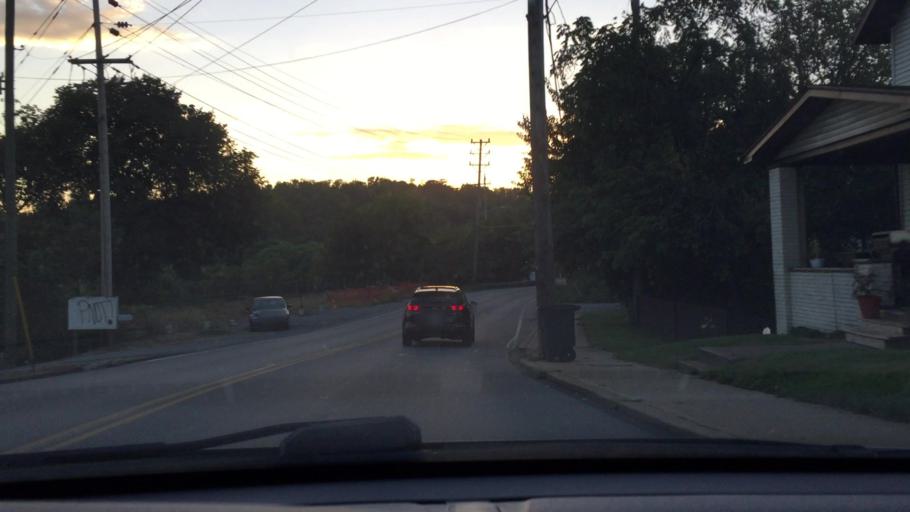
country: US
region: Pennsylvania
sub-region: Washington County
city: Canonsburg
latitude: 40.2579
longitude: -80.1975
